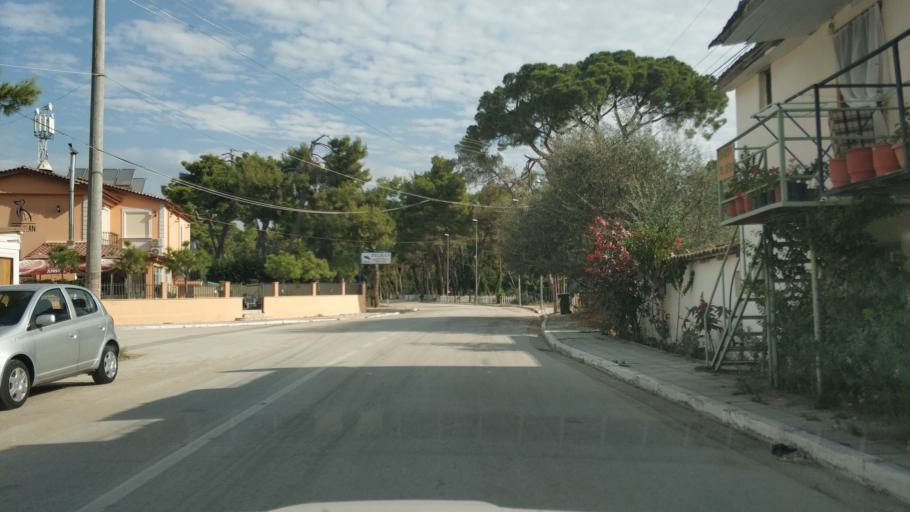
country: AL
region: Fier
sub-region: Rrethi i Lushnjes
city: Divjake
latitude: 40.9719
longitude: 19.4799
